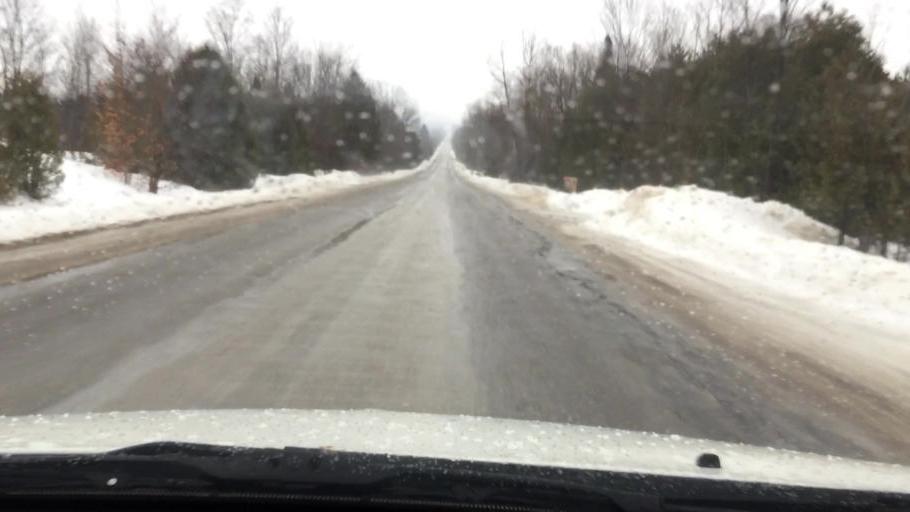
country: US
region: Michigan
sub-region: Charlevoix County
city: East Jordan
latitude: 45.1325
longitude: -85.1508
